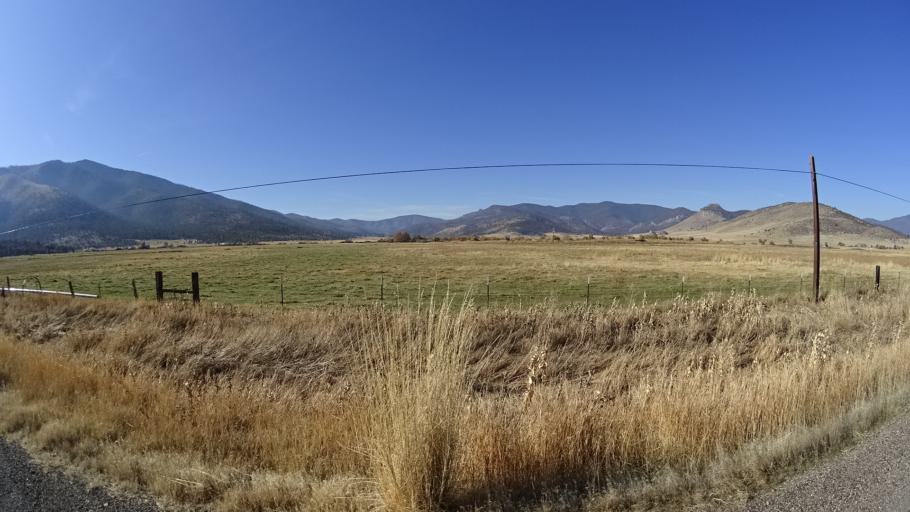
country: US
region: California
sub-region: Siskiyou County
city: Weed
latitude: 41.5030
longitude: -122.5154
